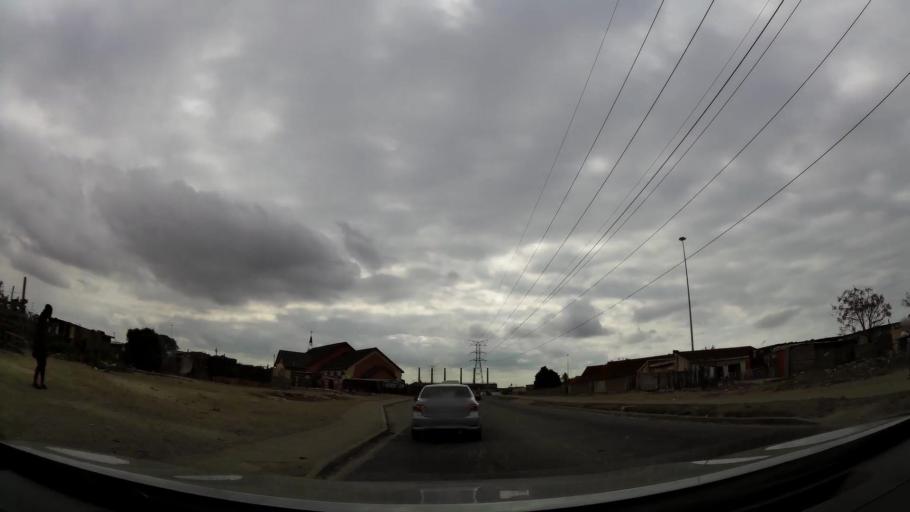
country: ZA
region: Eastern Cape
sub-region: Nelson Mandela Bay Metropolitan Municipality
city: Port Elizabeth
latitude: -33.8826
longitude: 25.5965
